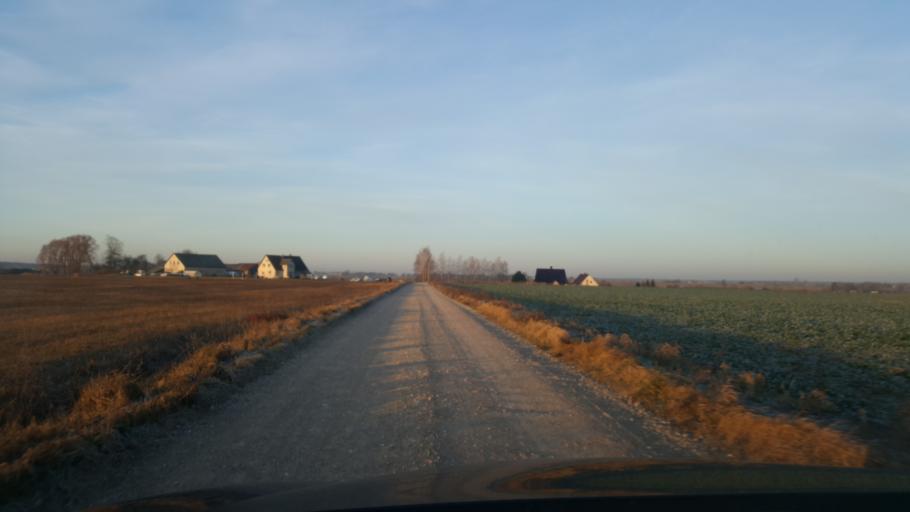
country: LT
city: Prienai
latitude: 54.4839
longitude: 23.9142
